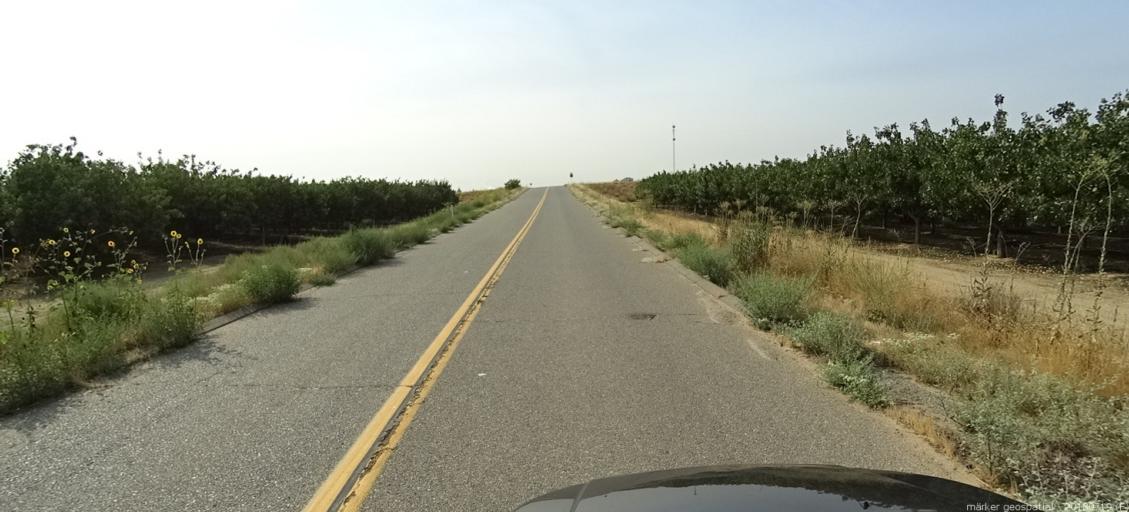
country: US
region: California
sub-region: Madera County
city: Fairmead
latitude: 37.0458
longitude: -120.1578
